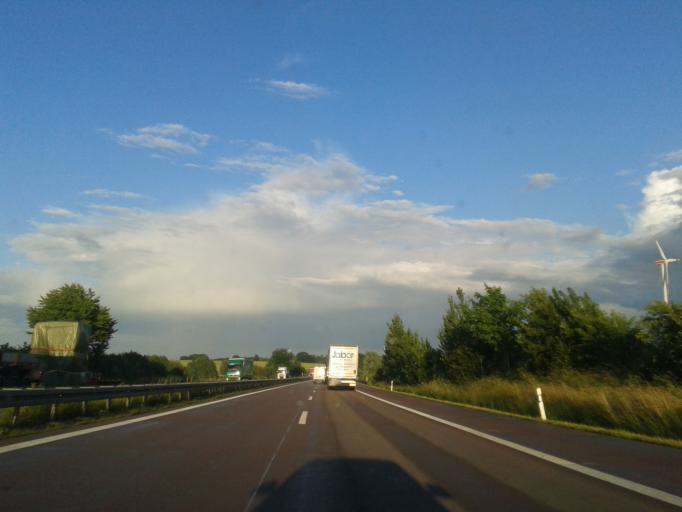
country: DE
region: Saxony
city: Bockelwitz
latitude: 51.2178
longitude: 12.9346
